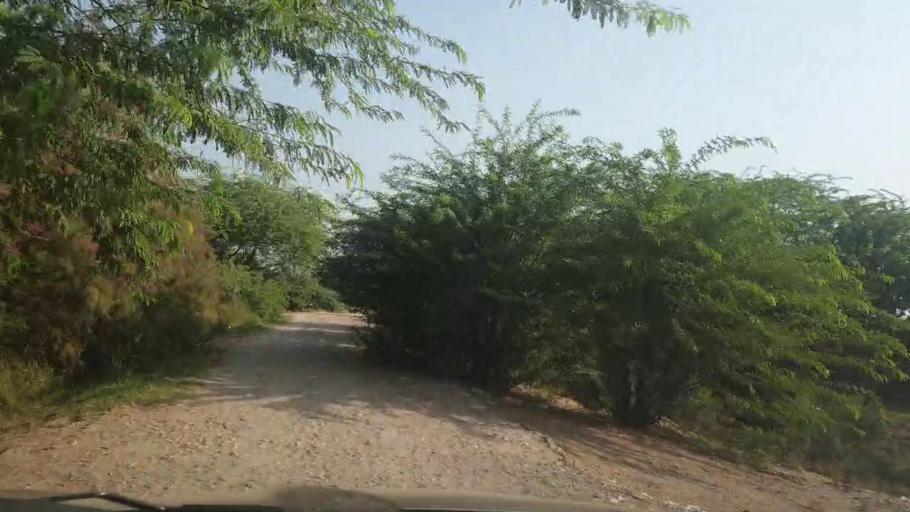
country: PK
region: Sindh
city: Larkana
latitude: 27.5976
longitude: 68.1598
